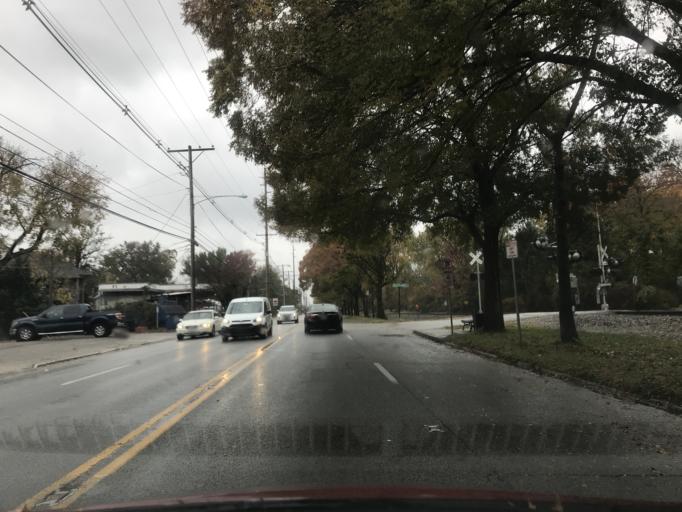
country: US
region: Kentucky
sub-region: Jefferson County
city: Saint Matthews
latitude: 38.2544
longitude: -85.6751
